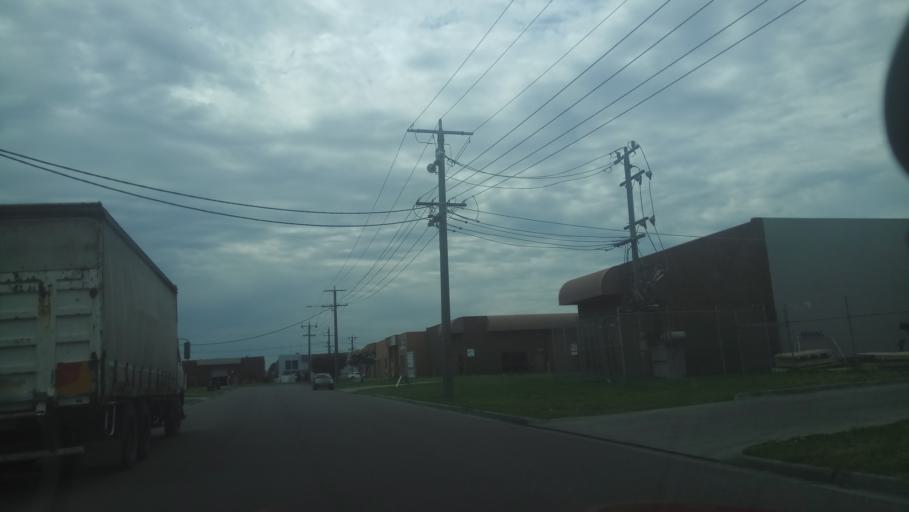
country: AU
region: Victoria
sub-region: Kingston
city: Aspendale Gardens
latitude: -38.0067
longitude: 145.1107
